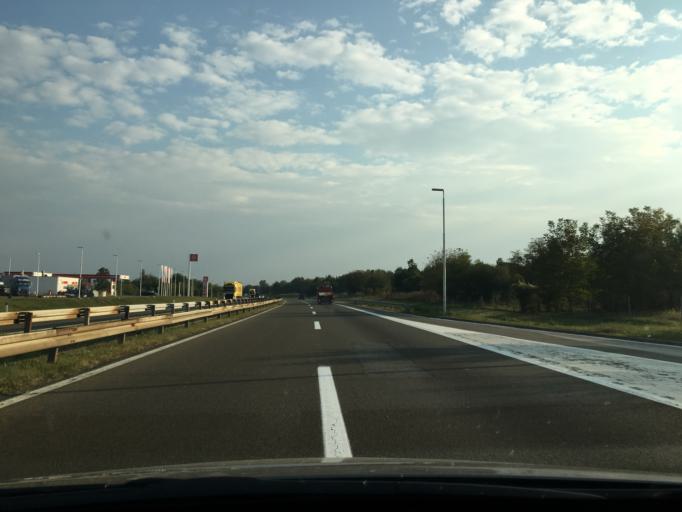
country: RS
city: Lugavcina
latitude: 44.5509
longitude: 20.9850
